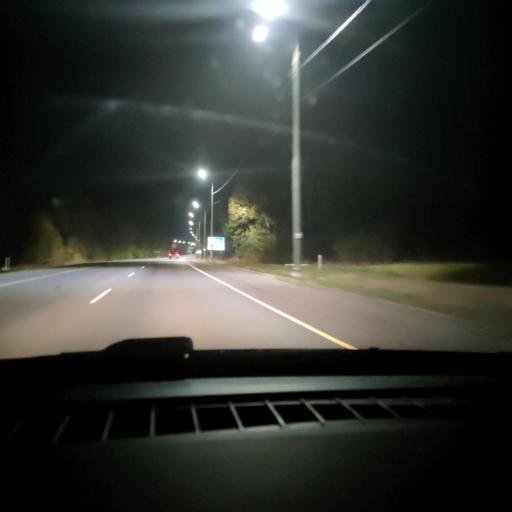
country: RU
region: Voronezj
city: Devitsa
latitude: 51.6353
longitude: 39.0009
